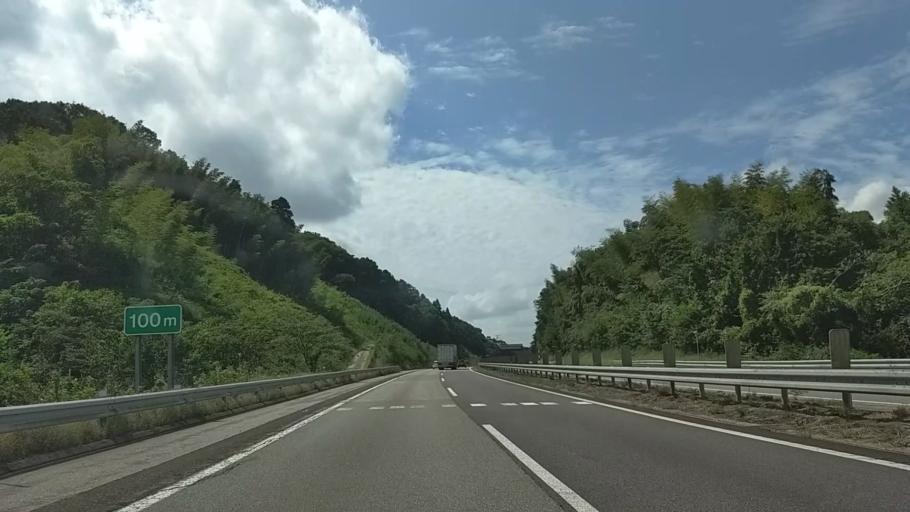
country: JP
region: Toyama
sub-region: Oyabe Shi
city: Oyabe
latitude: 36.6171
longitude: 136.8222
